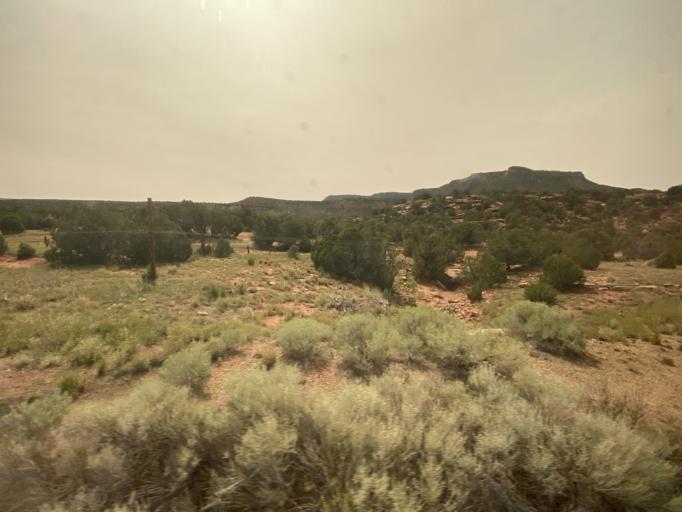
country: US
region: New Mexico
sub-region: San Miguel County
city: Pecos
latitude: 35.3969
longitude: -105.4921
